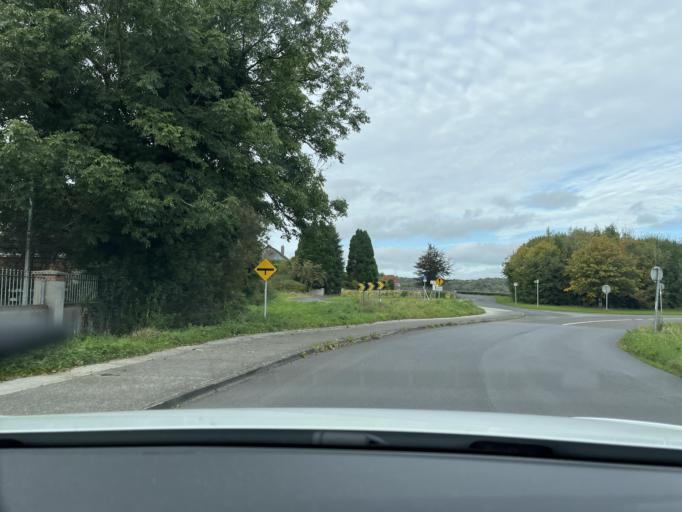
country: IE
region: Connaught
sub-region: Roscommon
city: Boyle
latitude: 53.9804
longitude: -8.2779
